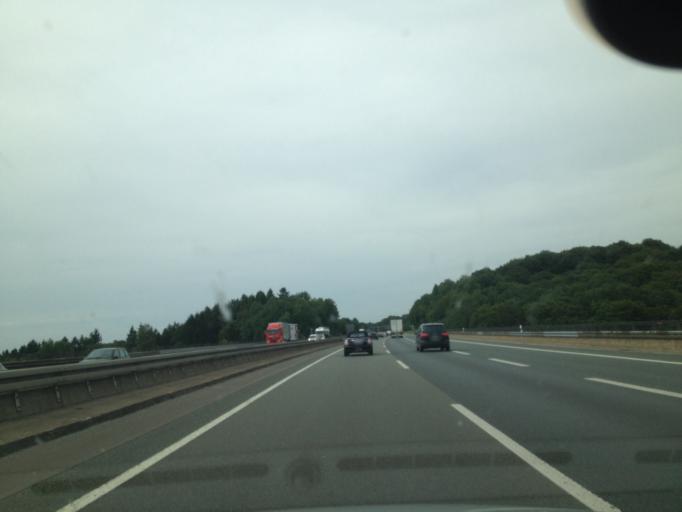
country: DE
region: North Rhine-Westphalia
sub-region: Regierungsbezirk Arnsberg
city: Luedenscheid
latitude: 51.2642
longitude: 7.6026
